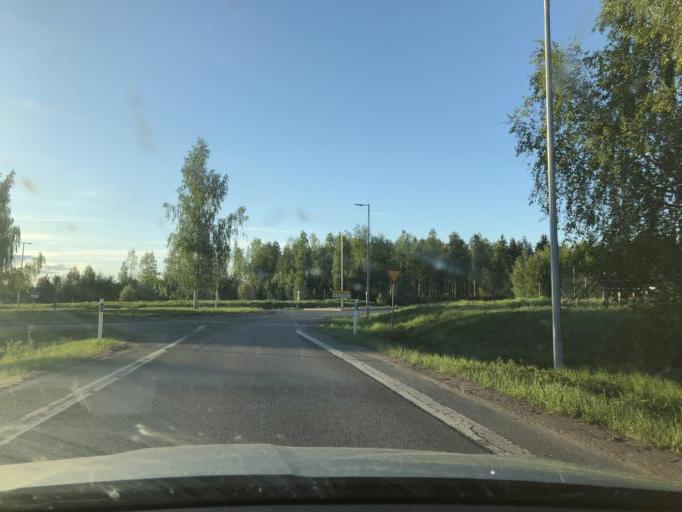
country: SE
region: Norrbotten
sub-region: Lulea Kommun
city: Sodra Sunderbyn
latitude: 65.6677
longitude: 21.9420
